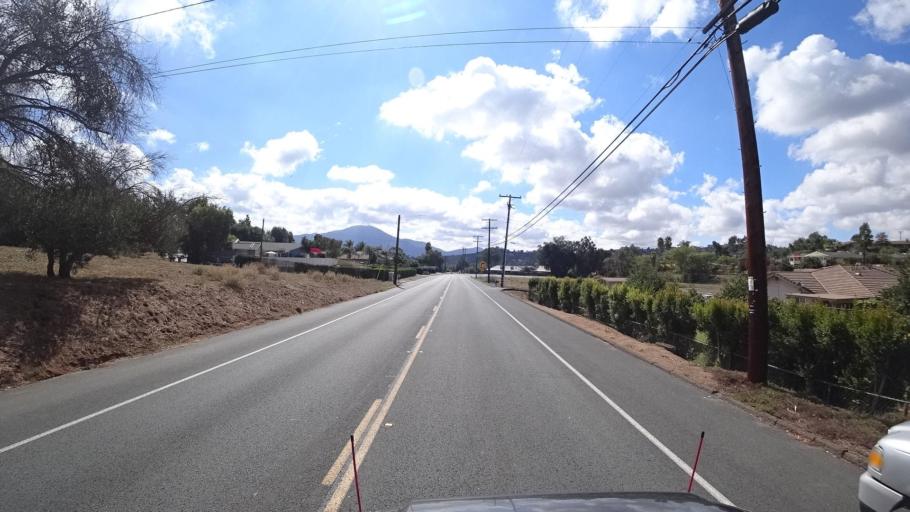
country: US
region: California
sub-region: San Diego County
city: Rancho San Diego
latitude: 32.7639
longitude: -116.9416
